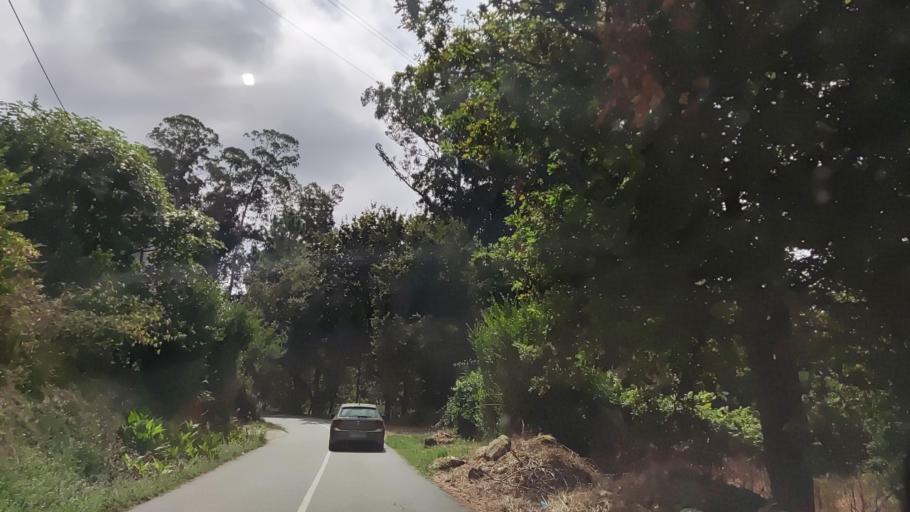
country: ES
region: Galicia
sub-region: Provincia da Coruna
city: Boiro
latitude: 42.6242
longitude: -8.8733
